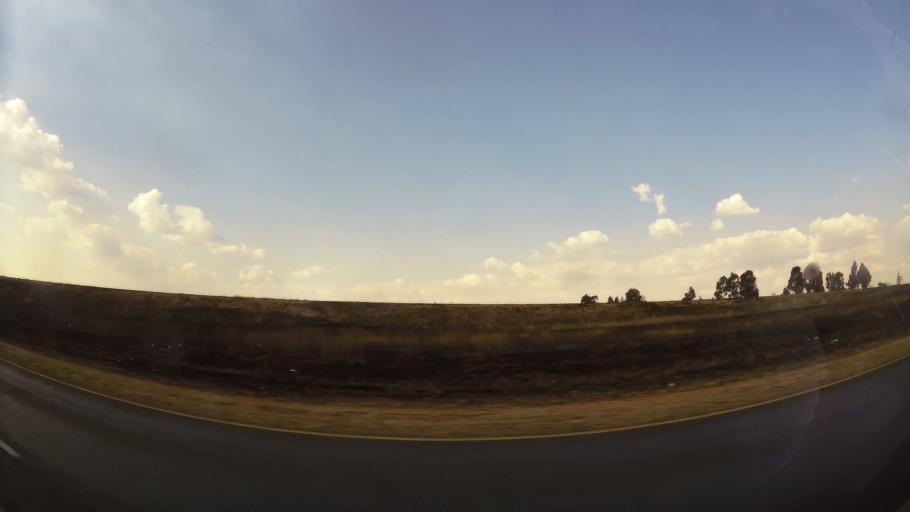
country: ZA
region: Gauteng
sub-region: Ekurhuleni Metropolitan Municipality
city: Springs
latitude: -26.3662
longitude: 28.3413
